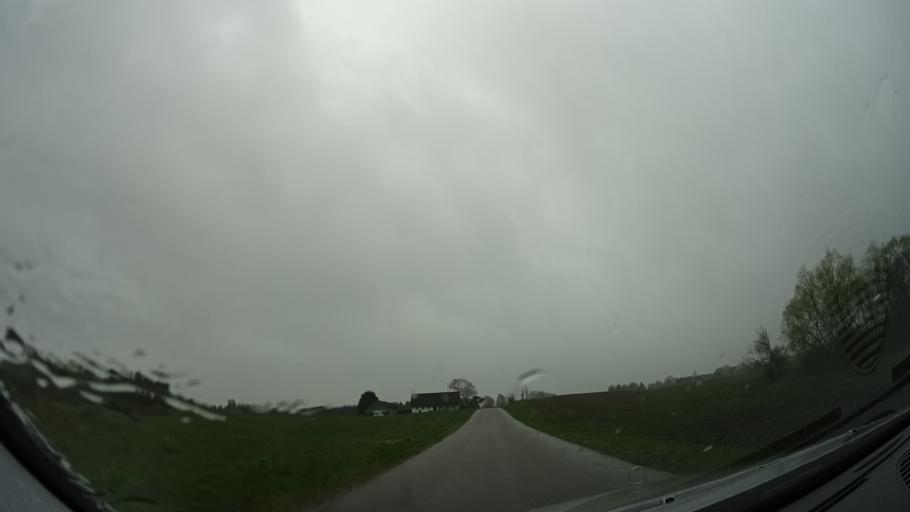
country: DK
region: Zealand
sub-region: Holbaek Kommune
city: Vipperod
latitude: 55.7114
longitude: 11.7731
